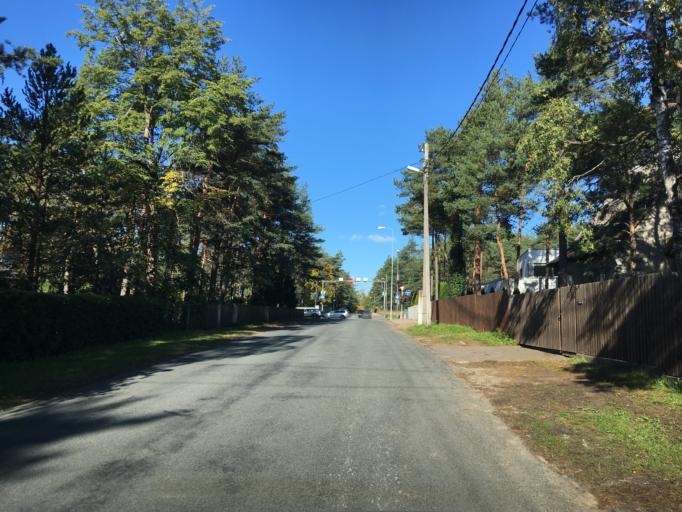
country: EE
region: Harju
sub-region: Saue vald
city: Laagri
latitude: 59.3744
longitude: 24.6741
